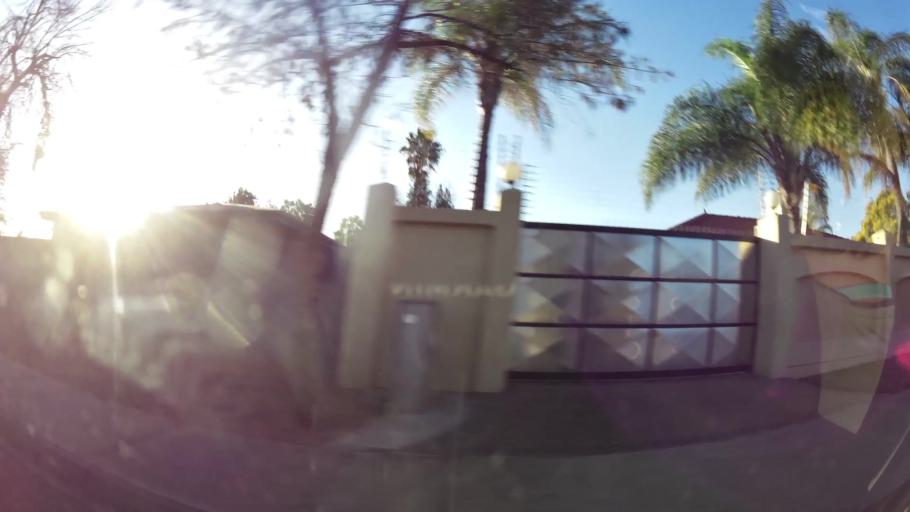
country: ZA
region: Gauteng
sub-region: City of Tshwane Metropolitan Municipality
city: Pretoria
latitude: -25.7060
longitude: 28.2110
